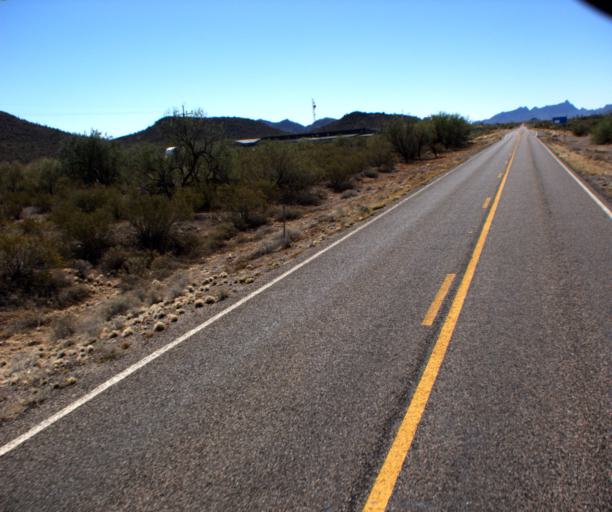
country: US
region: Arizona
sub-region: Pima County
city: Ajo
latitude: 32.2796
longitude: -112.7439
